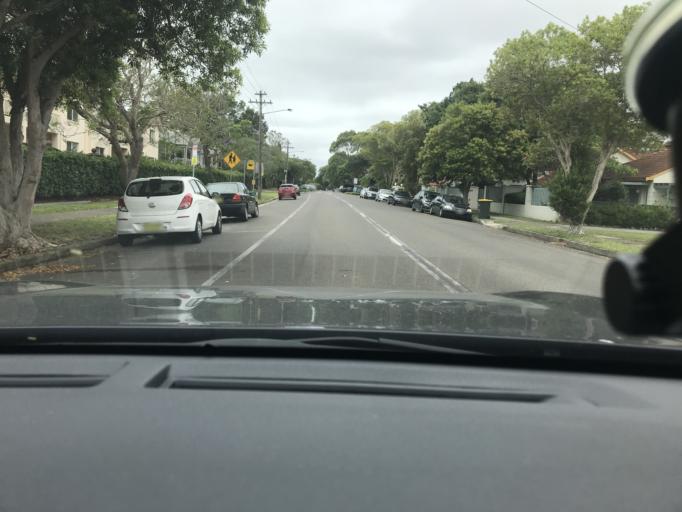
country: AU
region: New South Wales
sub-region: Canada Bay
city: Wareemba
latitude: -33.8585
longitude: 151.1174
